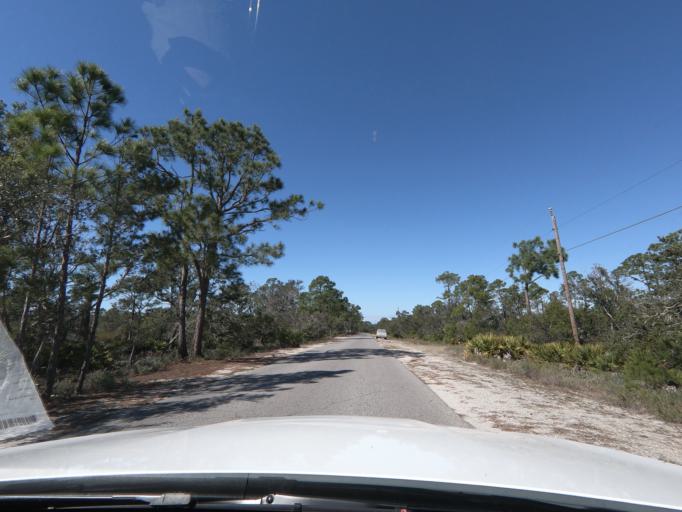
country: US
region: Florida
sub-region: Bay County
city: Lower Grand Lagoon
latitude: 30.1346
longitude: -85.7363
